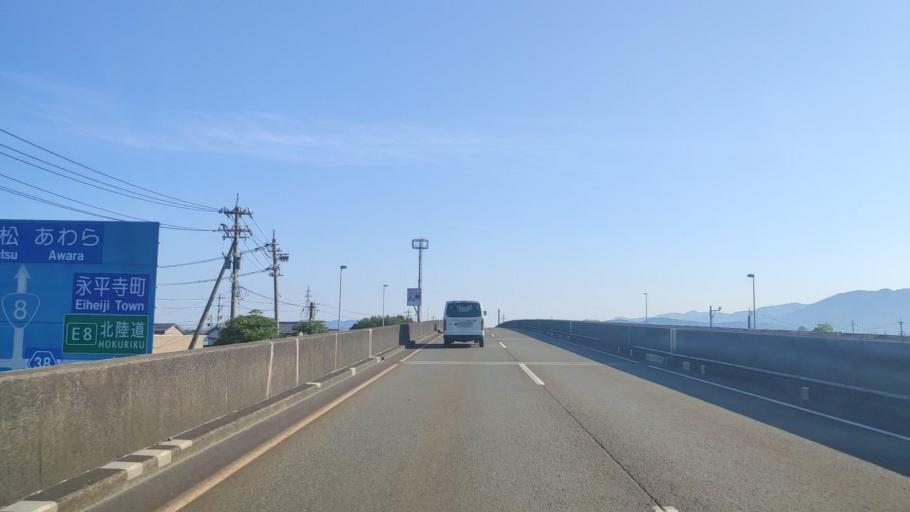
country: JP
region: Fukui
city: Maruoka
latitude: 36.1419
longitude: 136.2639
